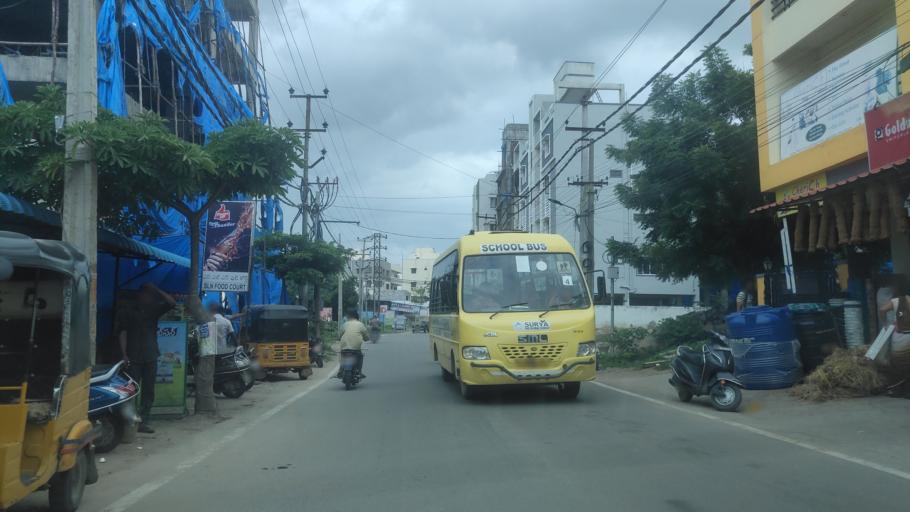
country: IN
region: Telangana
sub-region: Medak
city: Serilingampalle
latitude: 17.4995
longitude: 78.3491
